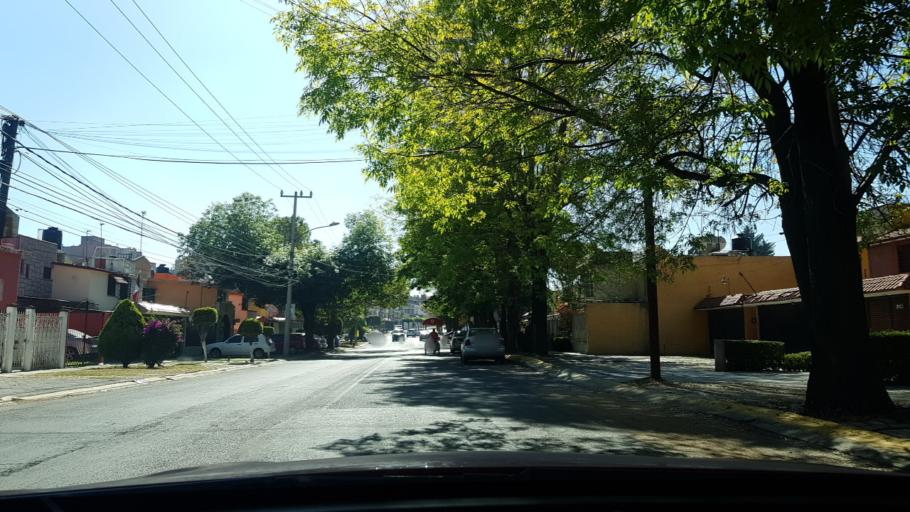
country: MX
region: Mexico
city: Cuautitlan Izcalli
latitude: 19.6481
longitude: -99.2013
